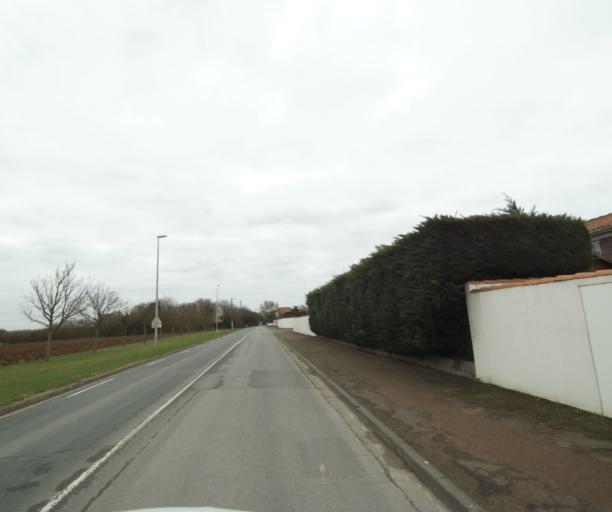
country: FR
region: Poitou-Charentes
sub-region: Departement de la Charente-Maritime
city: Nieul-sur-Mer
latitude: 46.1995
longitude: -1.1597
